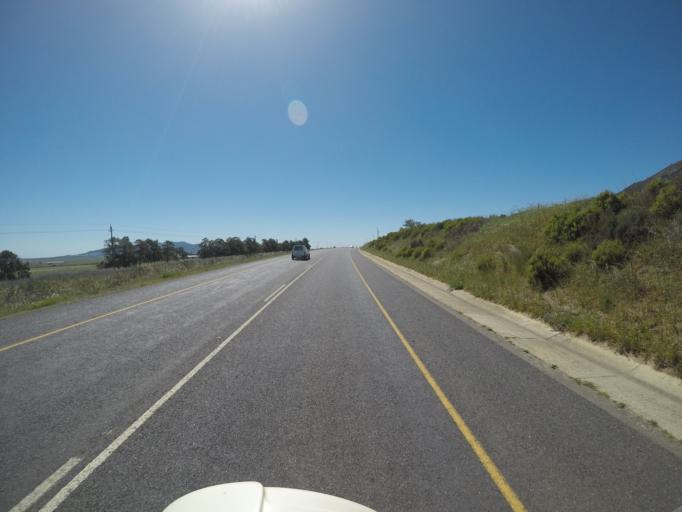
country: ZA
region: Western Cape
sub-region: Cape Winelands District Municipality
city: Noorder-Paarl
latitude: -33.7212
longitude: 18.8904
